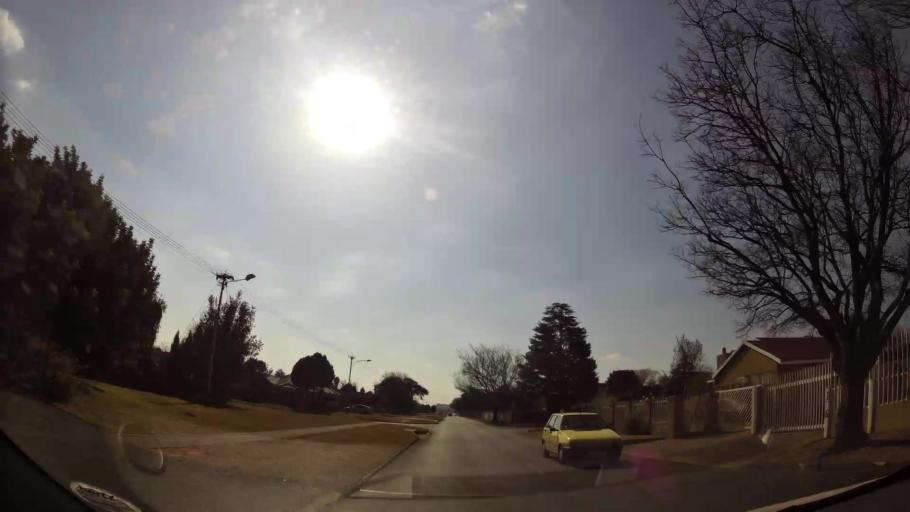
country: ZA
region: Gauteng
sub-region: West Rand District Municipality
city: Randfontein
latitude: -26.1559
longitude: 27.6917
